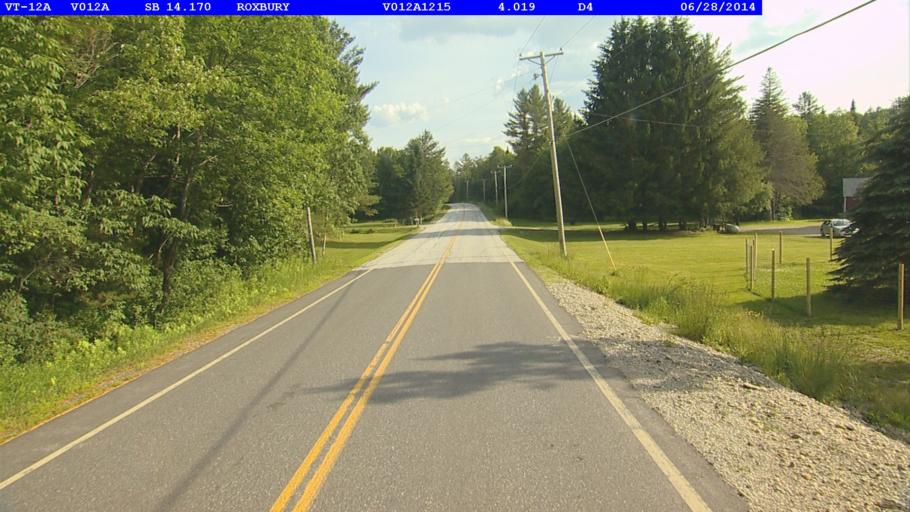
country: US
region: Vermont
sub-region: Washington County
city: Northfield
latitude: 44.0837
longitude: -72.7367
